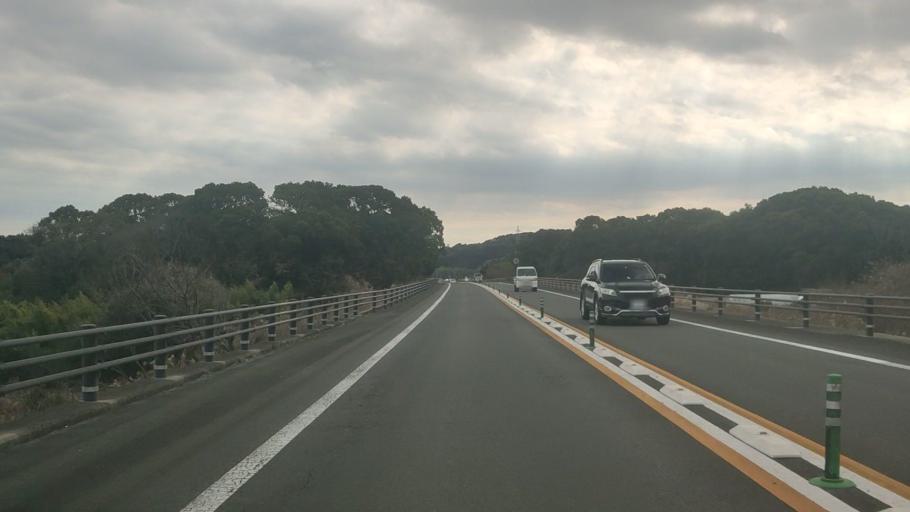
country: JP
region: Nagasaki
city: Shimabara
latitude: 32.7665
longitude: 130.3599
